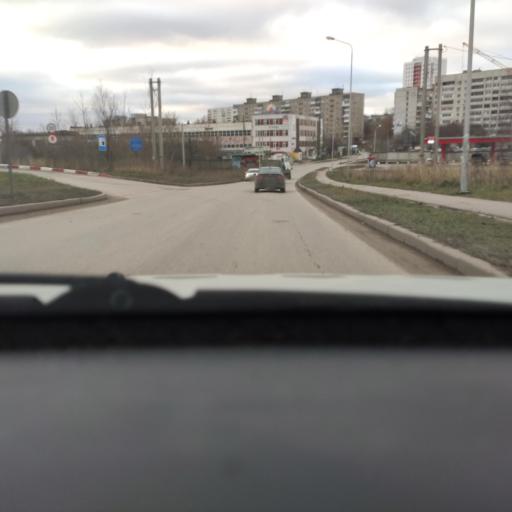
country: RU
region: Perm
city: Perm
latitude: 57.9823
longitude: 56.2805
